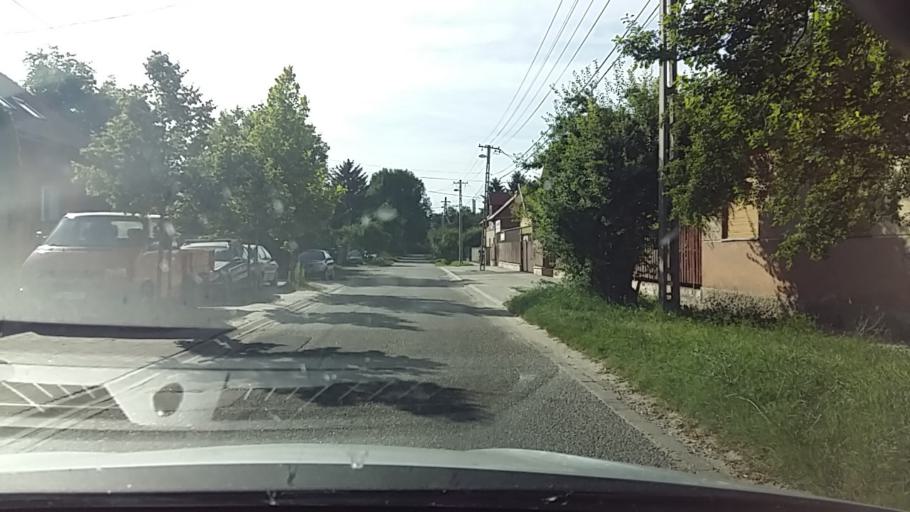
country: HU
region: Pest
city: God
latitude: 47.7001
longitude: 19.1455
